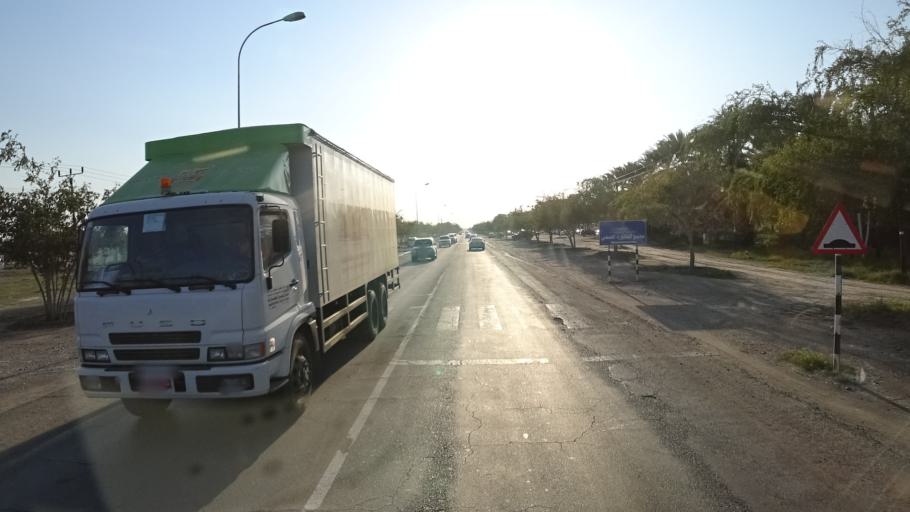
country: OM
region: Al Batinah
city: Al Khaburah
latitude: 23.9636
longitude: 57.0788
